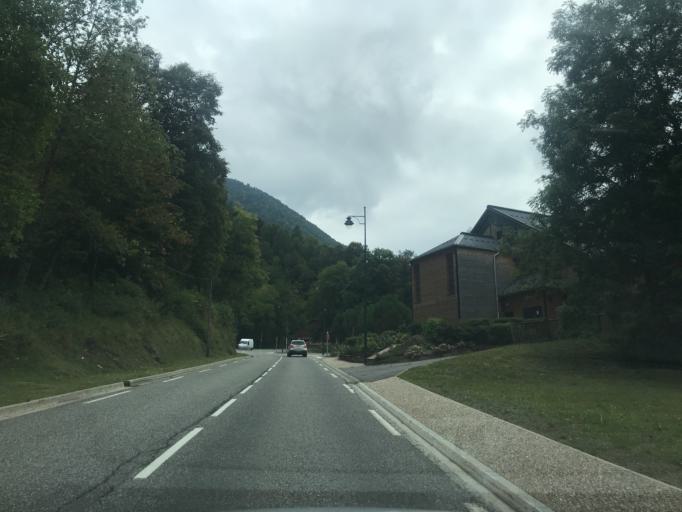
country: FR
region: Midi-Pyrenees
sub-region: Departement de la Haute-Garonne
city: Bagneres-de-Luchon
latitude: 42.7742
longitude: 0.6054
